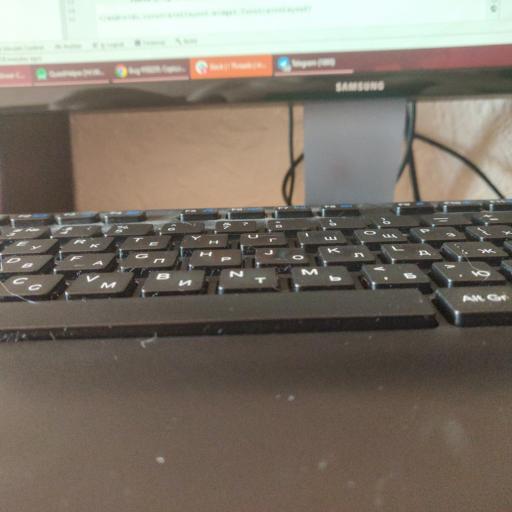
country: FI
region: Haeme
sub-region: Forssa
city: Jokioinen
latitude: 60.7924
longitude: 23.4661
